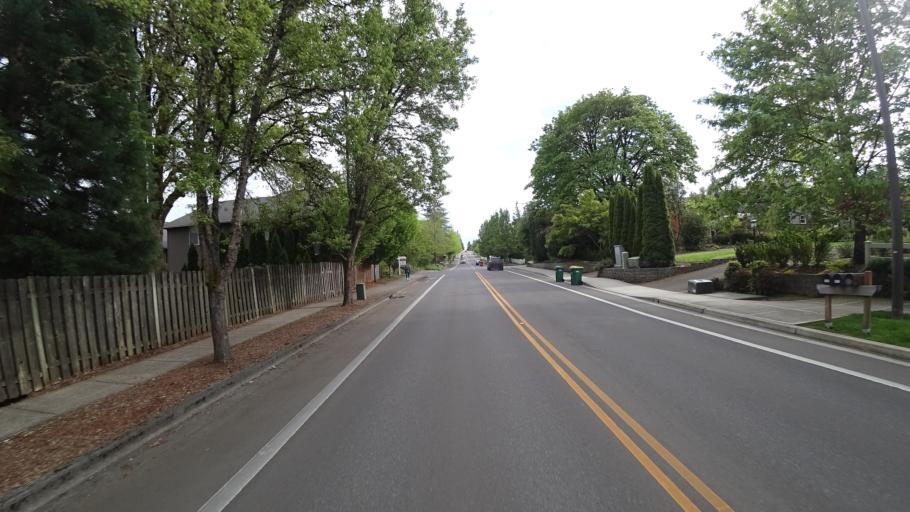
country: US
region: Oregon
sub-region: Washington County
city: Beaverton
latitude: 45.4561
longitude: -122.8362
